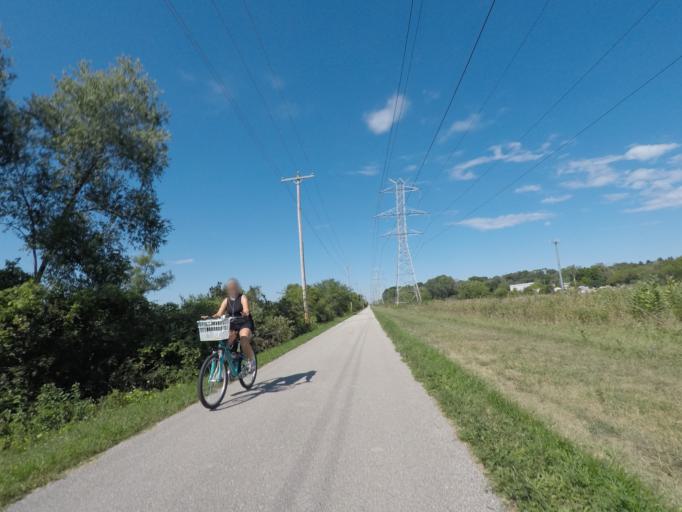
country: US
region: Wisconsin
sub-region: Waukesha County
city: New Berlin
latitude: 43.0100
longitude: -88.1612
